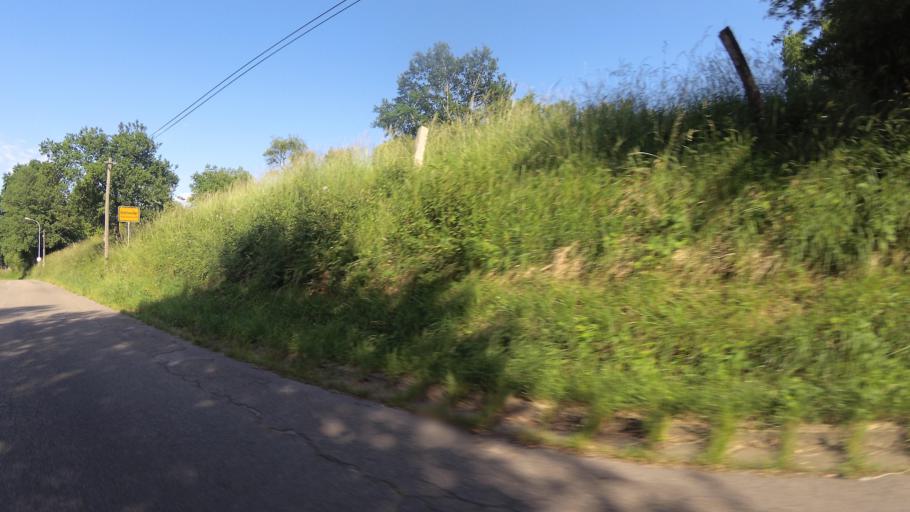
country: DE
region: Saarland
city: Blieskastel
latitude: 49.2357
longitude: 7.3075
